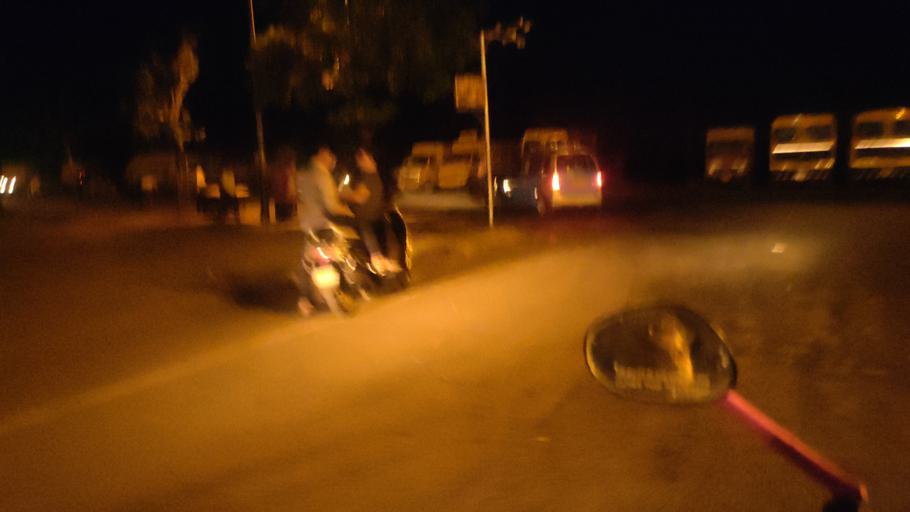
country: IN
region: Maharashtra
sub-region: Thane
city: Bhayandar
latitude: 19.2988
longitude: 72.8409
